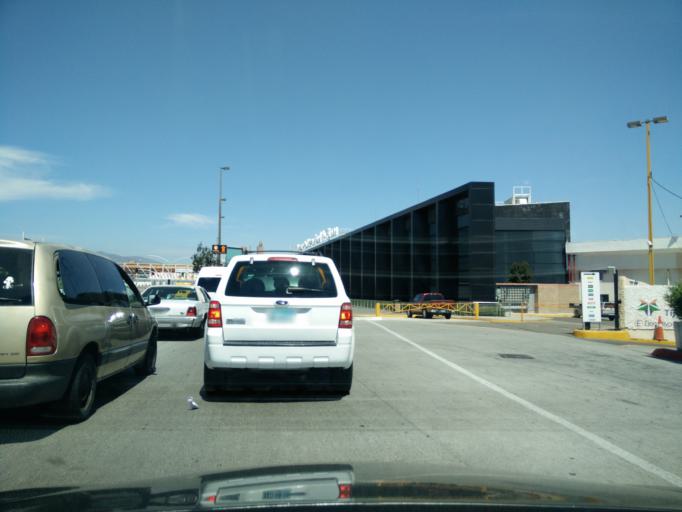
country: MX
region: Baja California
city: Tijuana
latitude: 32.5466
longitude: -116.9773
